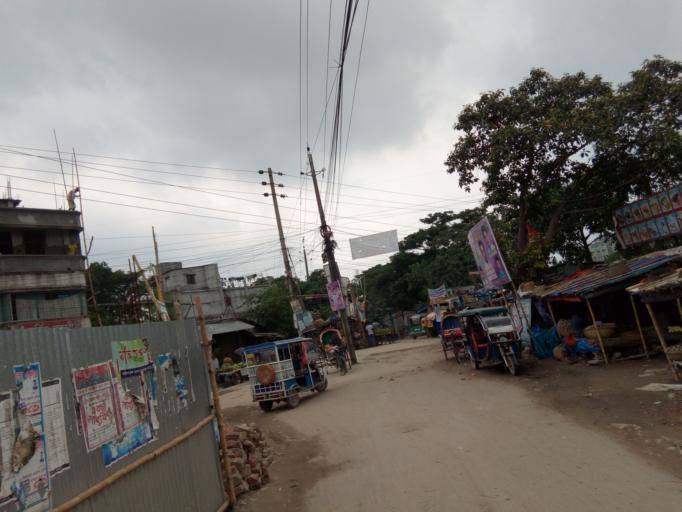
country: BD
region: Dhaka
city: Paltan
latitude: 23.7111
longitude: 90.4877
